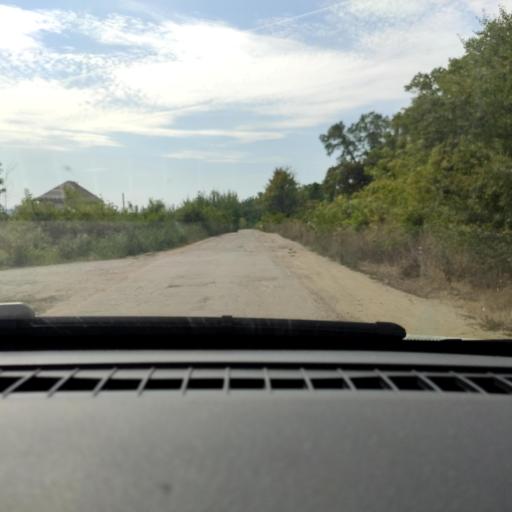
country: RU
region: Voronezj
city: Pridonskoy
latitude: 51.7485
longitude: 39.0753
